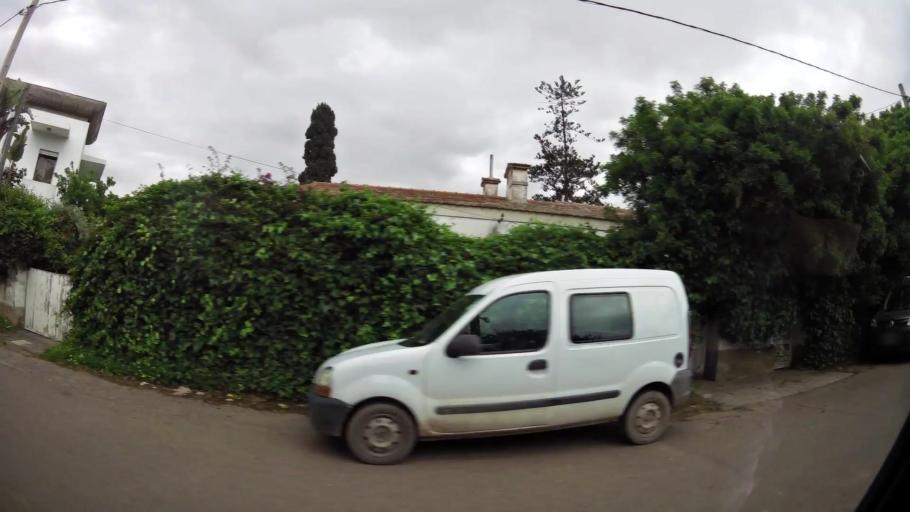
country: MA
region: Grand Casablanca
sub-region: Casablanca
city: Casablanca
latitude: 33.5780
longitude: -7.6626
